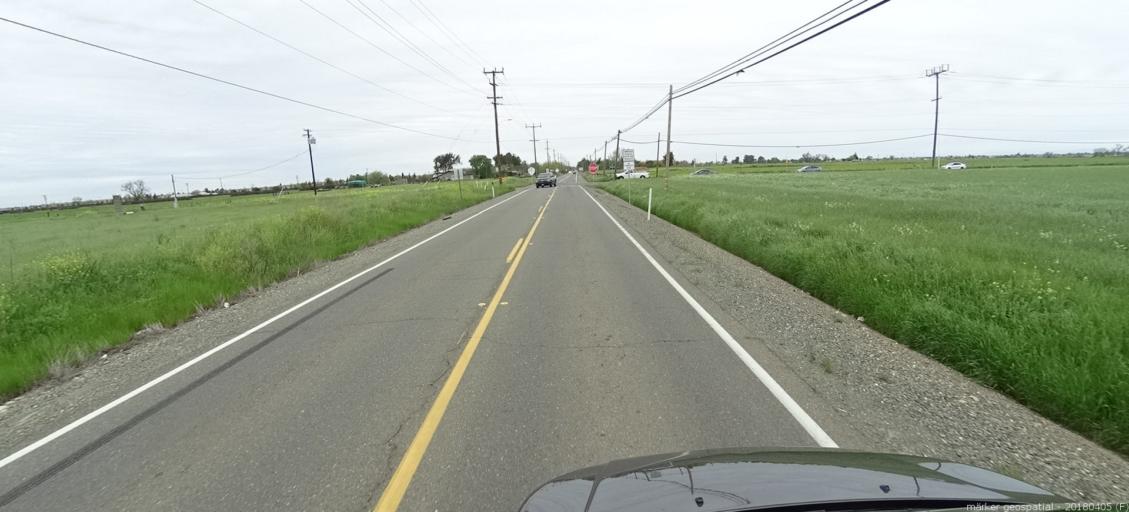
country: US
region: California
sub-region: Sacramento County
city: Laguna
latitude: 38.3715
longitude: -121.4176
